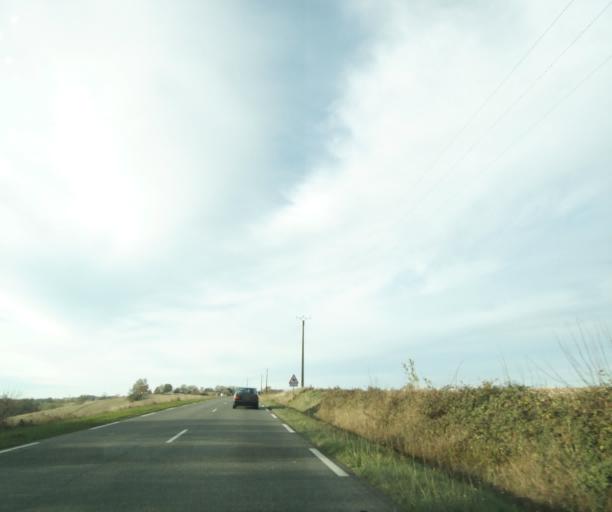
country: FR
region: Midi-Pyrenees
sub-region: Departement du Gers
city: Eauze
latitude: 43.7849
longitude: 0.1116
